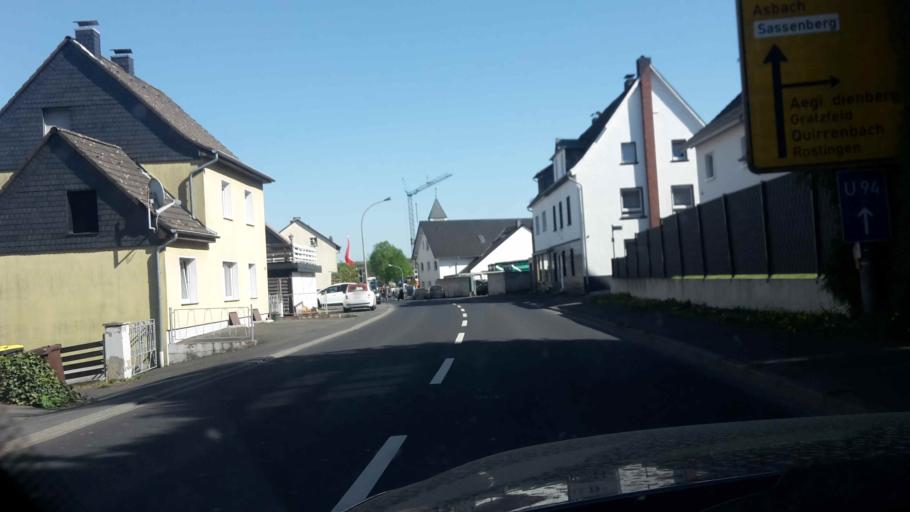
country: DE
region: Rheinland-Pfalz
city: Windhagen
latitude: 50.6884
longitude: 7.3355
